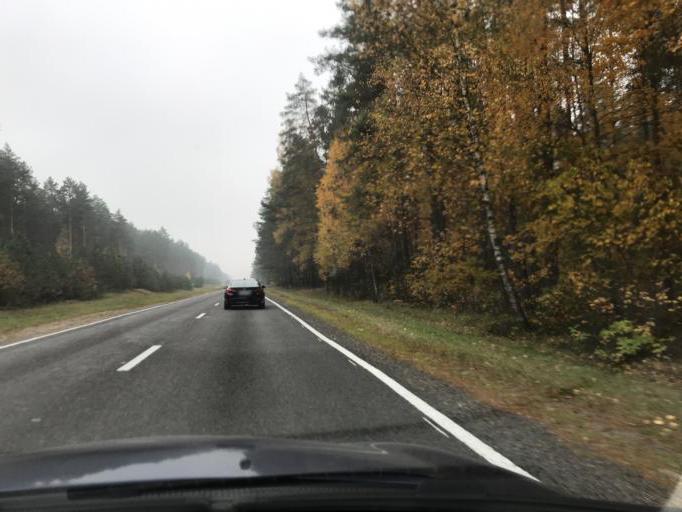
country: LT
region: Alytaus apskritis
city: Druskininkai
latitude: 53.8674
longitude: 23.8941
